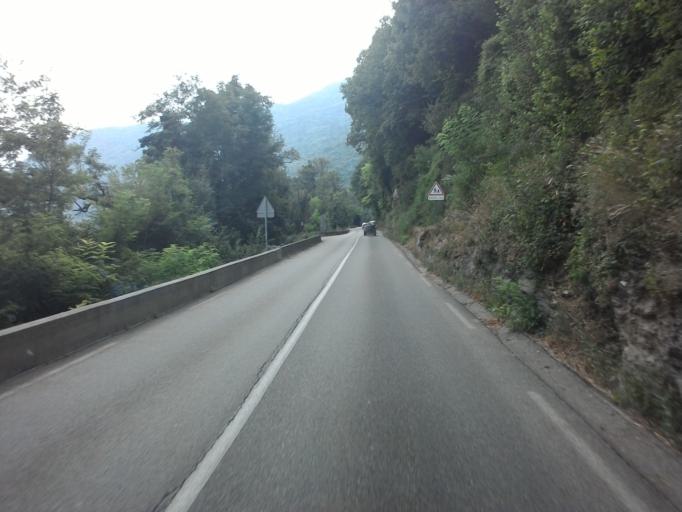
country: FR
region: Rhone-Alpes
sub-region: Departement de l'Isere
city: Notre-Dame-de-Mesage
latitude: 45.0694
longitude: 5.7557
